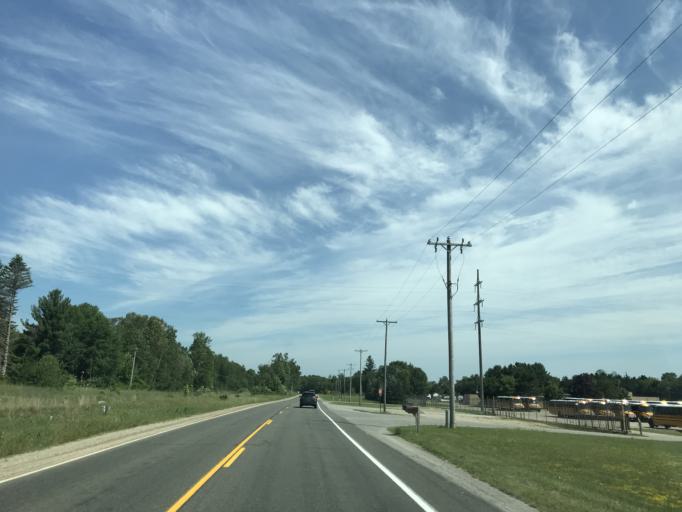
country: US
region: Michigan
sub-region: Grand Traverse County
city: Traverse City
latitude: 44.7035
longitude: -85.6258
